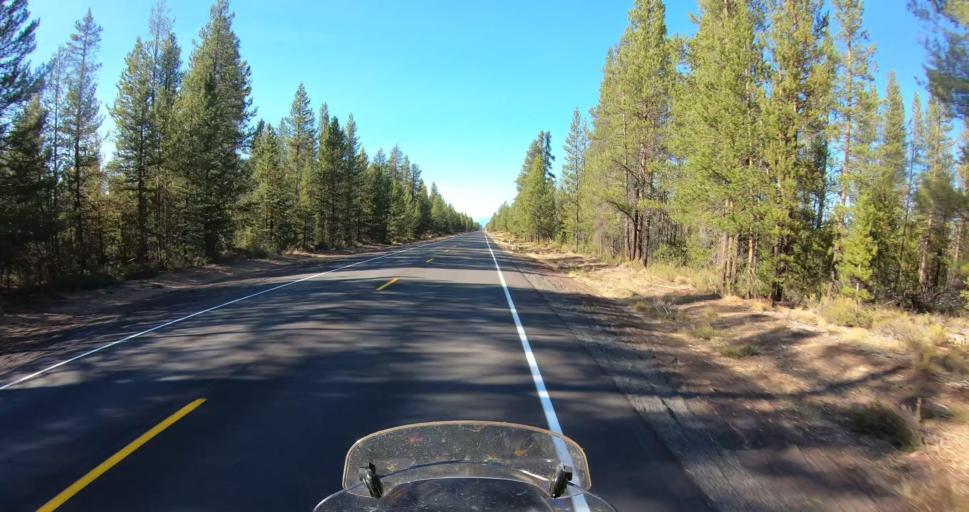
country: US
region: Oregon
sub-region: Deschutes County
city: La Pine
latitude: 43.5285
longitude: -121.4599
